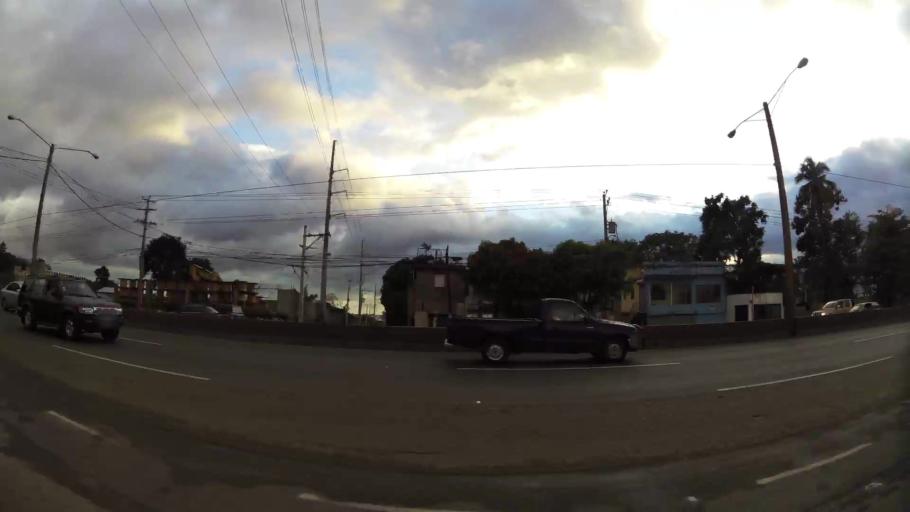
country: DO
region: Santo Domingo
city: Santo Domingo Oeste
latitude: 18.5045
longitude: -70.0010
